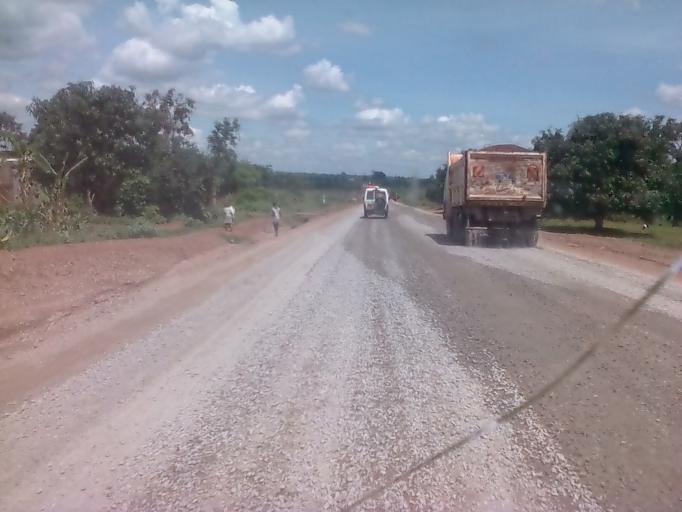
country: UG
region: Eastern Region
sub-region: Mbale District
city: Mbale
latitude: 1.0748
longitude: 34.1614
